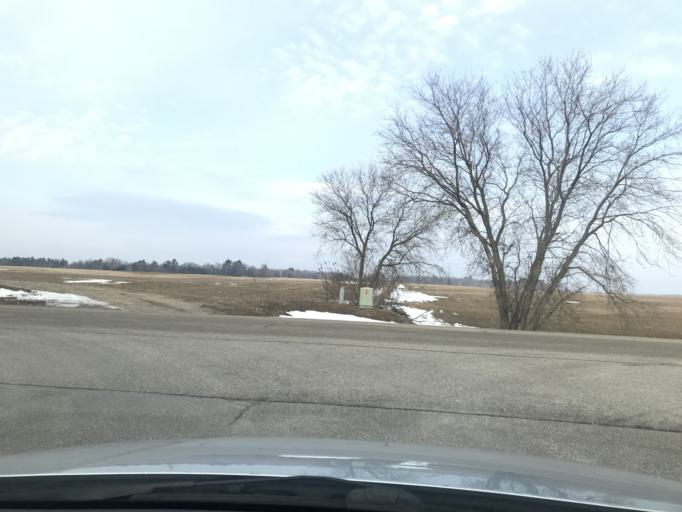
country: US
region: Wisconsin
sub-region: Oconto County
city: Oconto Falls
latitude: 44.8299
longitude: -88.1883
